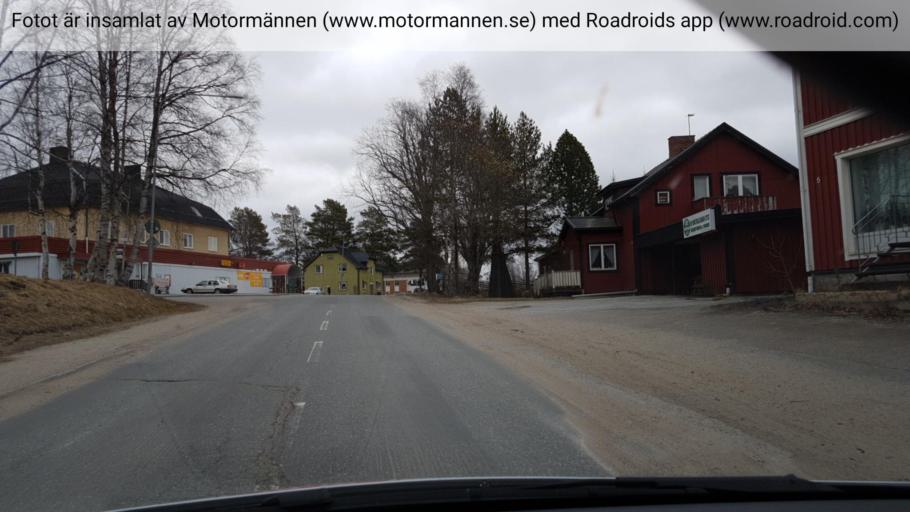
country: SE
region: Vaesternorrland
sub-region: OErnskoeldsviks Kommun
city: Ornskoldsvik
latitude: 63.5512
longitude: 18.5969
